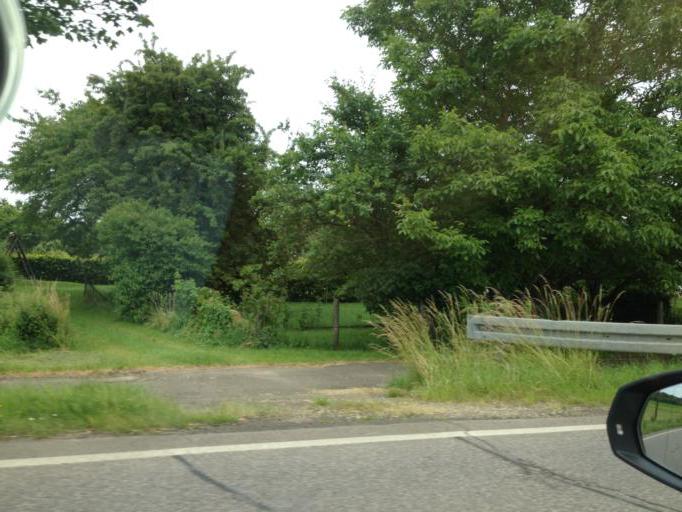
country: DE
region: Saarland
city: Orscholz
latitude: 49.4723
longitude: 6.4737
